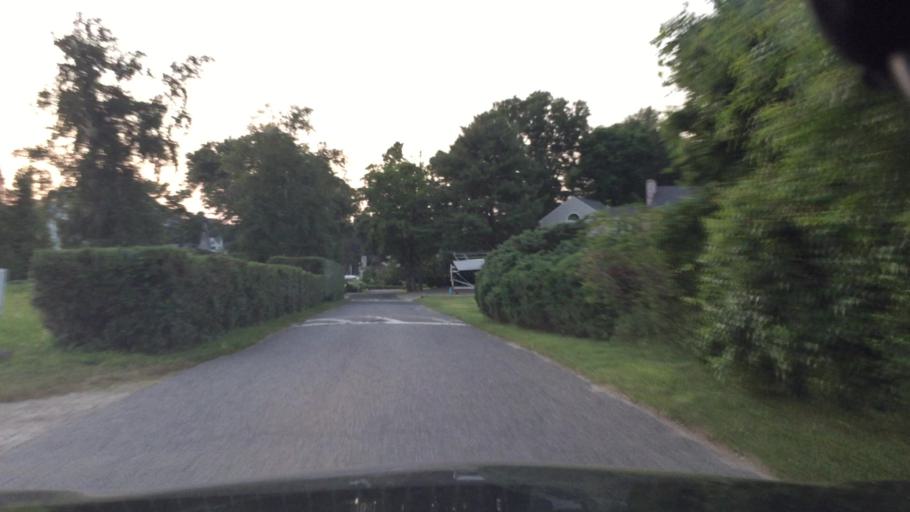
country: US
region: Connecticut
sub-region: Fairfield County
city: Darien
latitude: 41.0659
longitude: -73.4297
